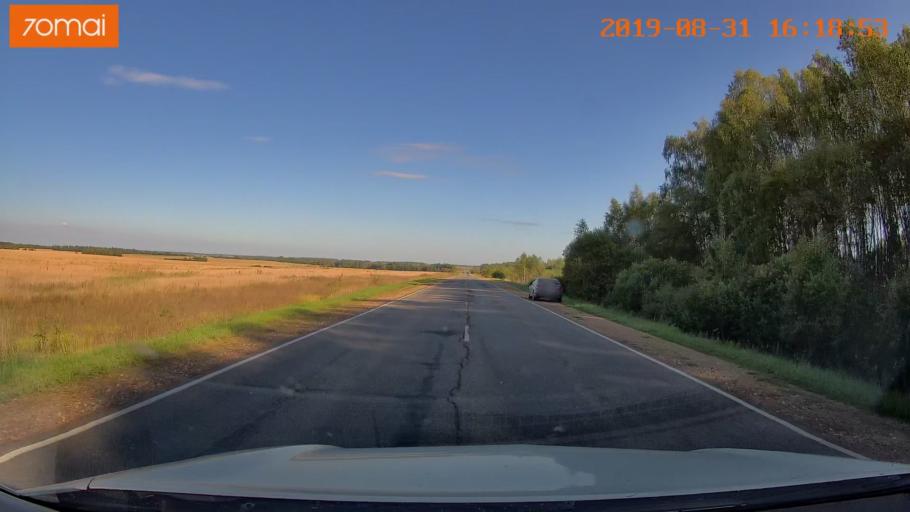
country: RU
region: Kaluga
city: Nikola-Lenivets
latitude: 54.5331
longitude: 35.5648
